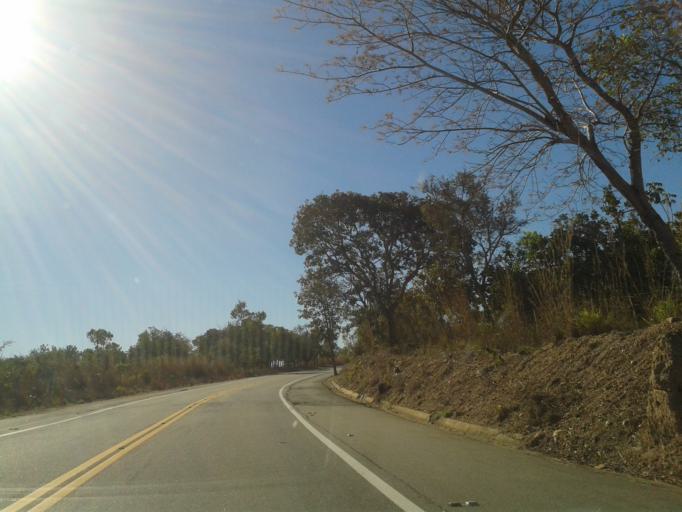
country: BR
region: Goias
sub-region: Itapuranga
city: Itapuranga
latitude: -15.3881
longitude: -50.3902
